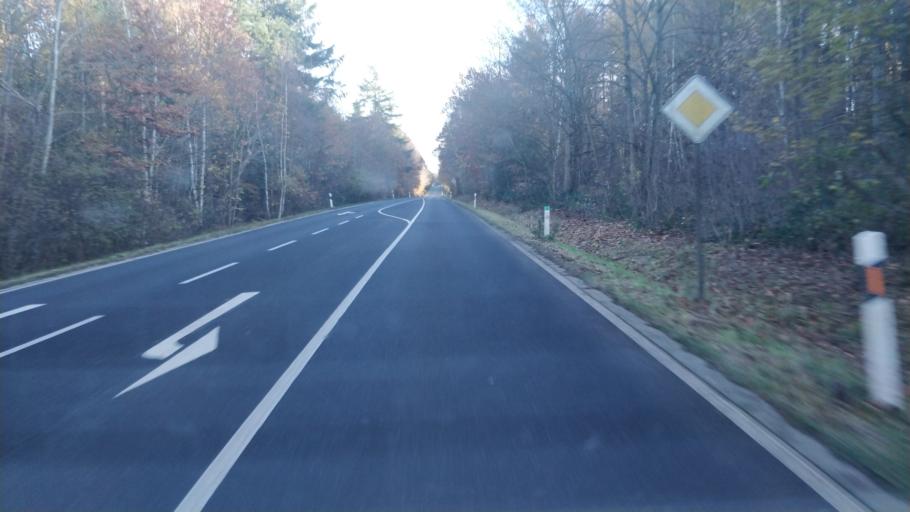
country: DE
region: North Rhine-Westphalia
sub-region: Regierungsbezirk Koln
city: Rheinbach
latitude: 50.6182
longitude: 6.8936
